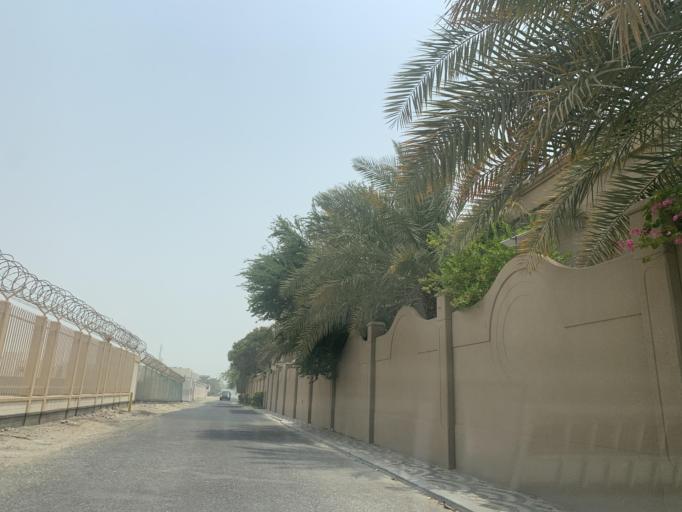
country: BH
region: Central Governorate
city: Madinat Hamad
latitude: 26.1665
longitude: 50.4792
